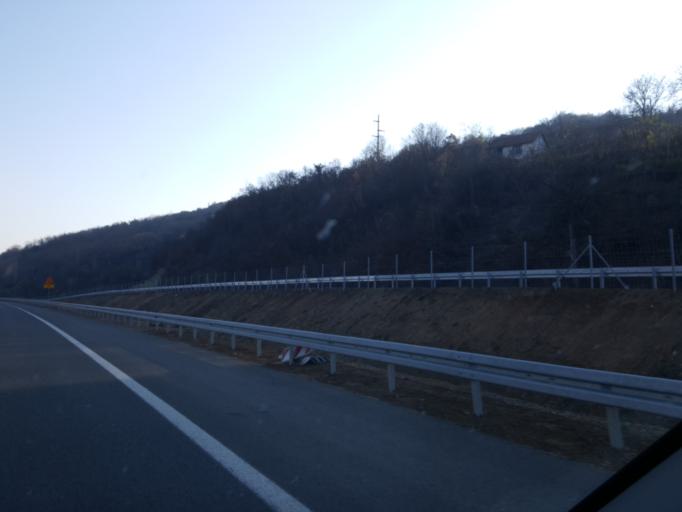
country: RS
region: Central Serbia
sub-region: Pirotski Okrug
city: Pirot
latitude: 43.1811
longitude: 22.5670
